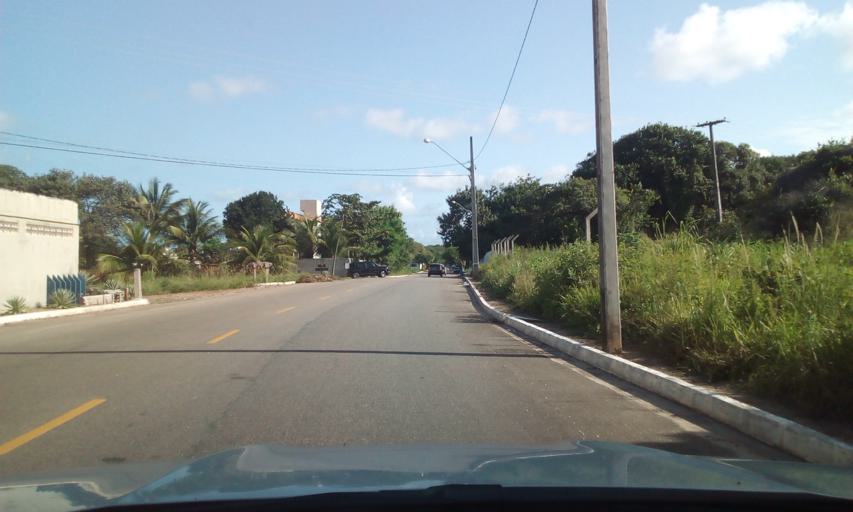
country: BR
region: Paraiba
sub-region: Joao Pessoa
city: Joao Pessoa
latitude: -7.1551
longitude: -34.7954
